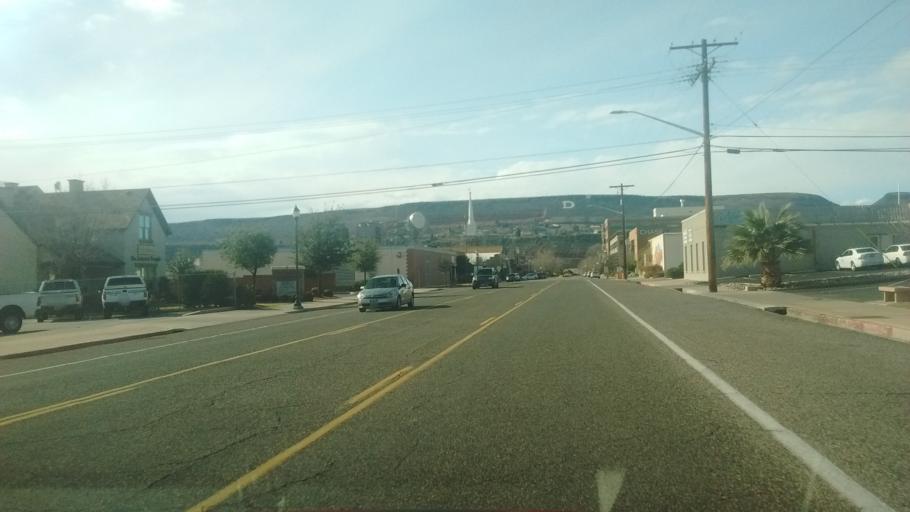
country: US
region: Utah
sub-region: Washington County
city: Saint George
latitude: 37.1082
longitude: -113.5796
